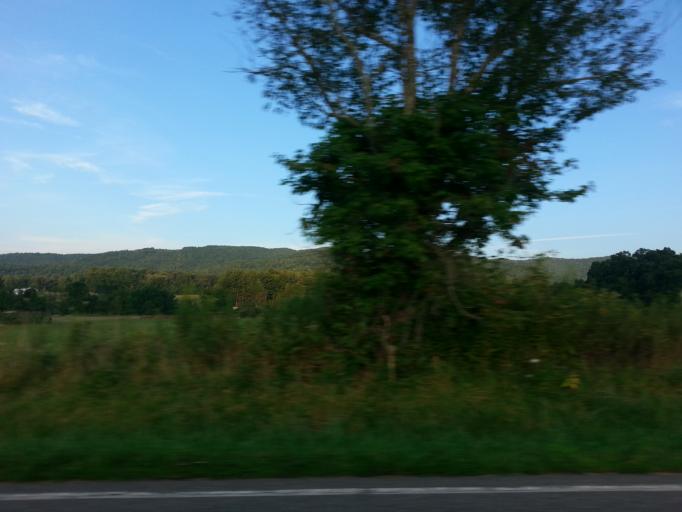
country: US
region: Tennessee
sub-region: Johnson County
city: Mountain City
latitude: 36.4989
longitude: -81.9401
